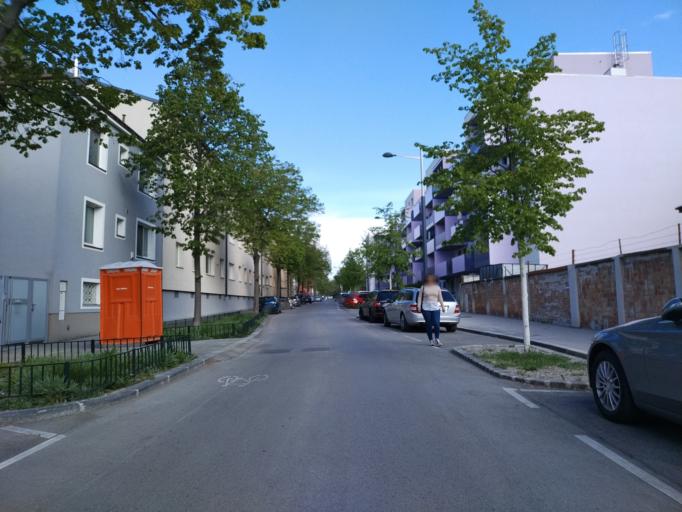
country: AT
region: Lower Austria
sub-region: Politischer Bezirk Modling
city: Vosendorf
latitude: 48.1595
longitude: 16.3110
